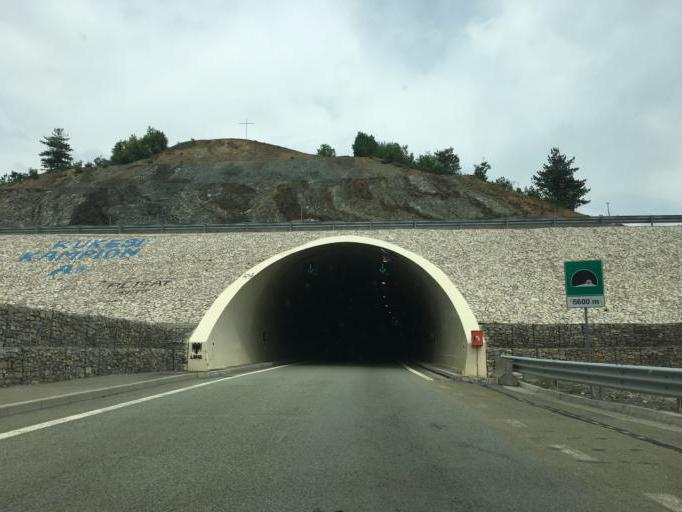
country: AL
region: Lezhe
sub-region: Rrethi i Lezhes
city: Shengjin
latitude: 42.0039
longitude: 20.2283
